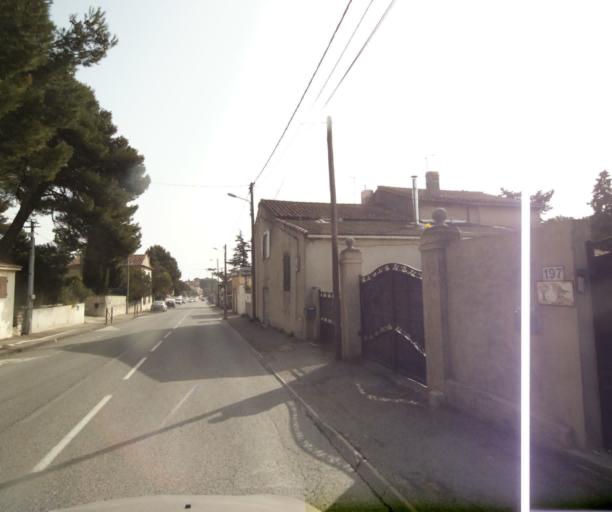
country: FR
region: Provence-Alpes-Cote d'Azur
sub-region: Departement des Bouches-du-Rhone
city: Marseille 15
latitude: 43.3900
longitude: 5.3443
